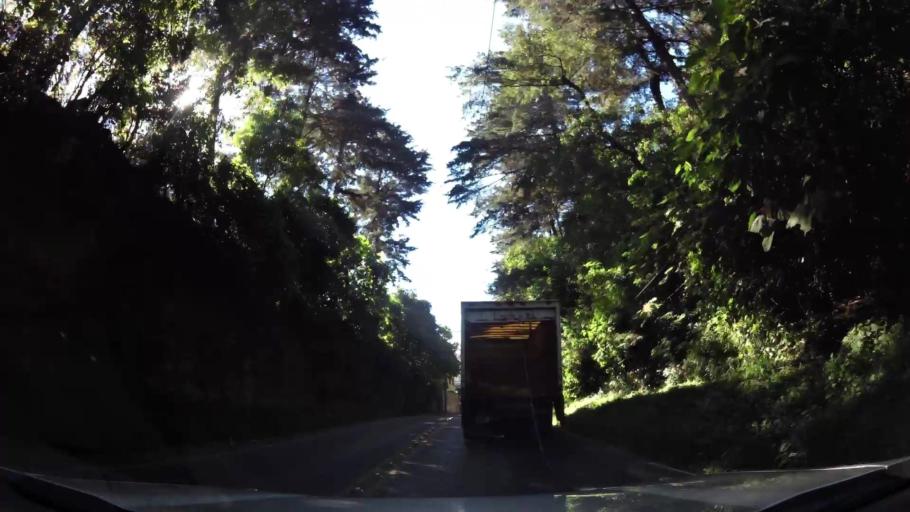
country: GT
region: Sacatepequez
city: Santa Lucia Milpas Altas
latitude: 14.5831
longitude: -90.6609
